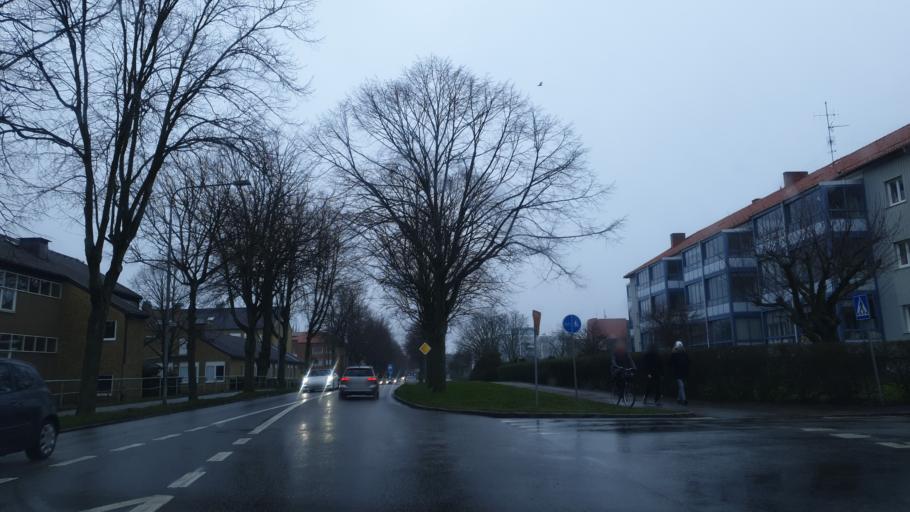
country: SE
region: Skane
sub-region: Trelleborgs Kommun
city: Trelleborg
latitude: 55.3793
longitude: 13.1647
